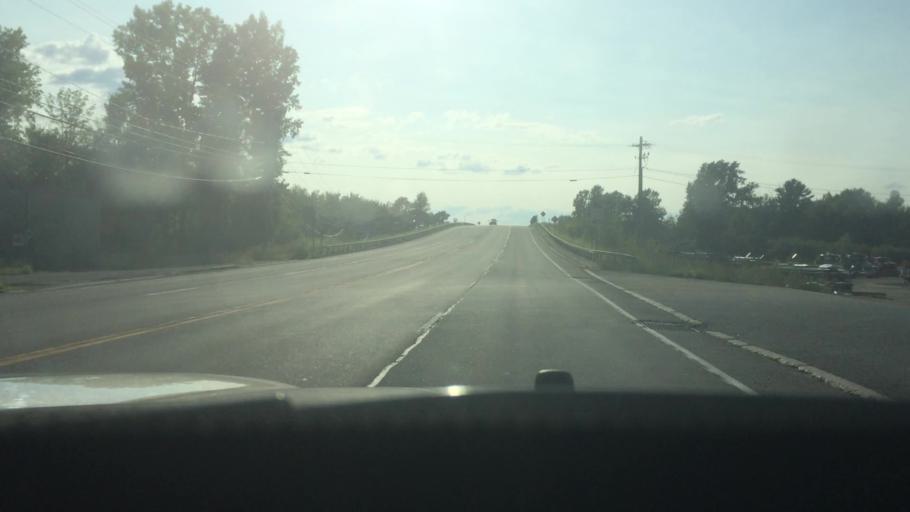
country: US
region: New York
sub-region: St. Lawrence County
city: Potsdam
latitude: 44.6673
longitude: -75.0054
